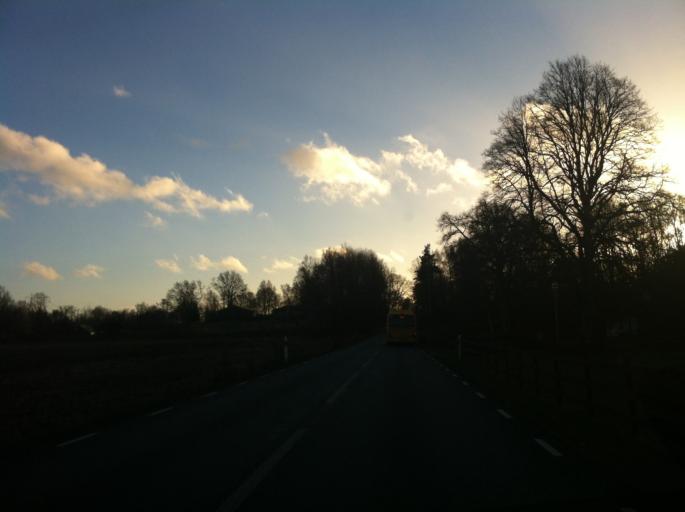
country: SE
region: Skane
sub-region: Hassleholms Kommun
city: Hastveda
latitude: 56.1846
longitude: 13.9525
